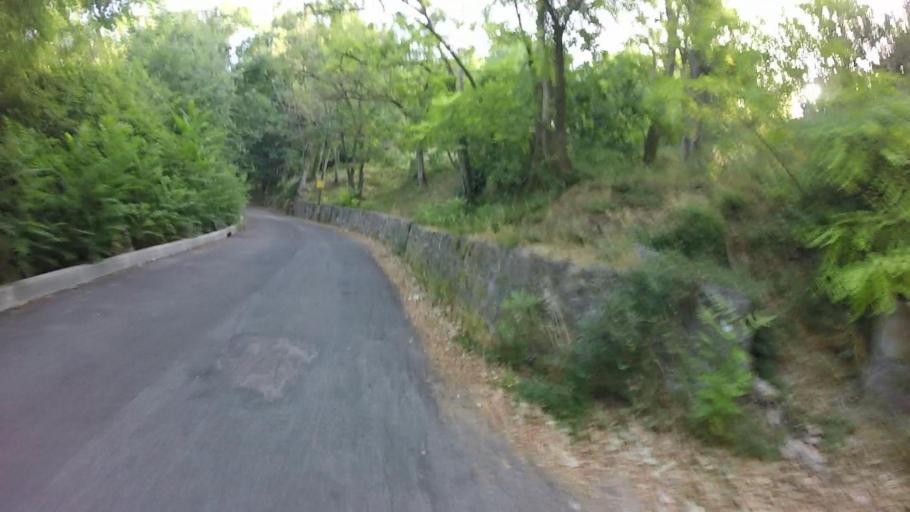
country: FR
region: Provence-Alpes-Cote d'Azur
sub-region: Departement des Alpes-Maritimes
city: Mouans-Sartoux
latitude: 43.6332
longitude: 6.9768
